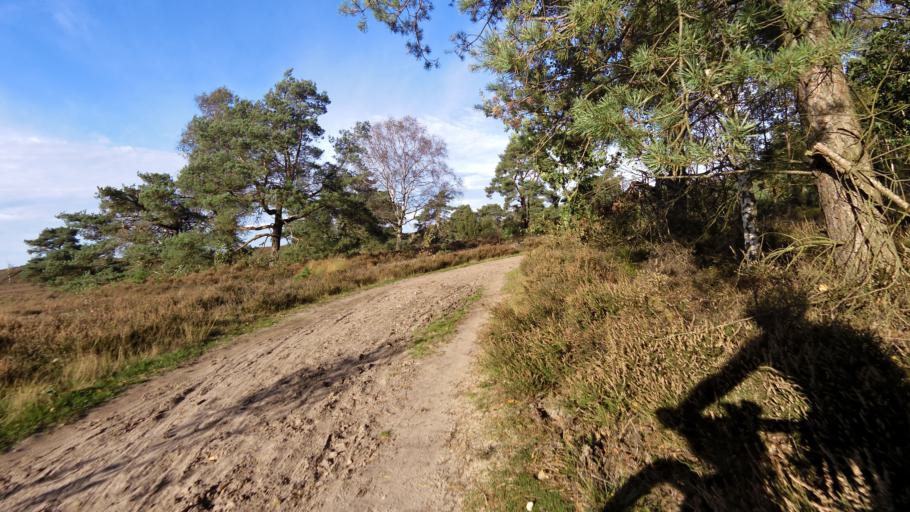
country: NL
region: Gelderland
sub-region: Gemeente Epe
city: Epe
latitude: 52.3753
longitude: 5.9937
